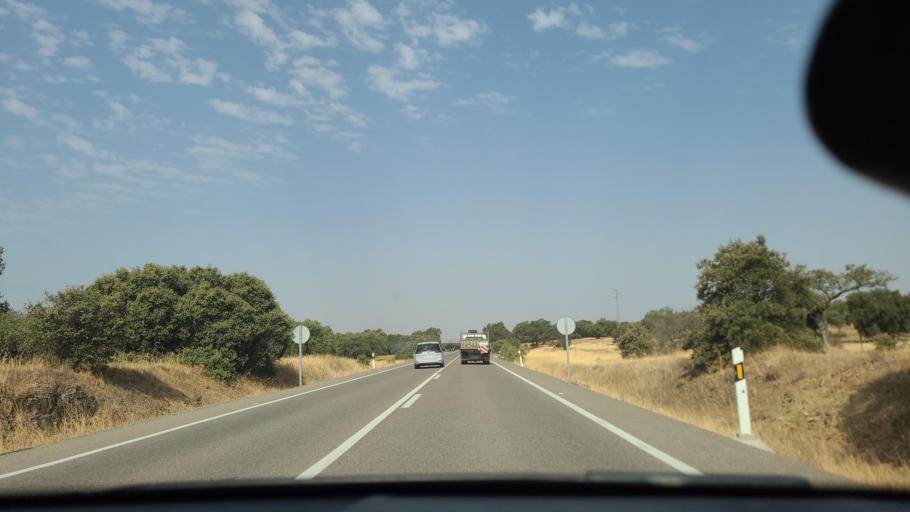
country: ES
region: Andalusia
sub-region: Province of Cordoba
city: Fuente Obejuna
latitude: 38.2613
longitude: -5.4832
